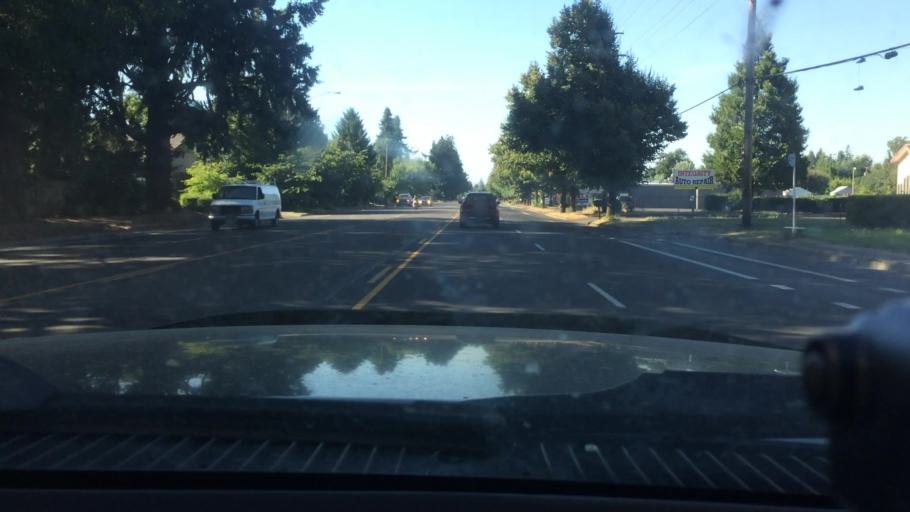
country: US
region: Oregon
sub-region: Lane County
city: Eugene
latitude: 44.0690
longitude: -123.1180
